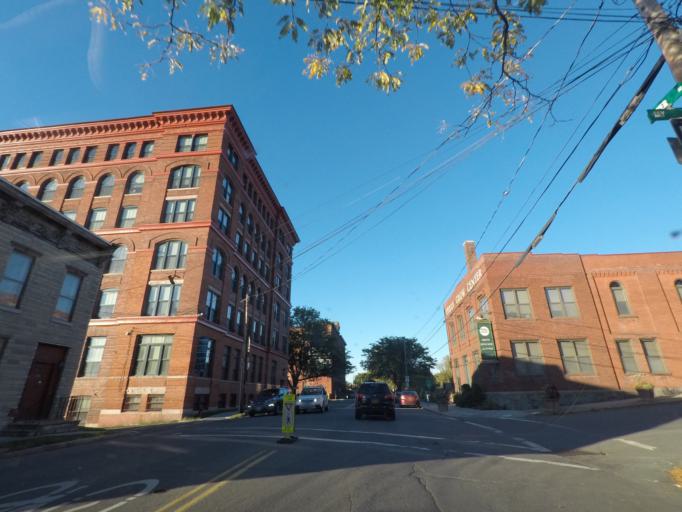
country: US
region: New York
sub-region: Albany County
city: Green Island
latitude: 42.7418
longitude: -73.6854
